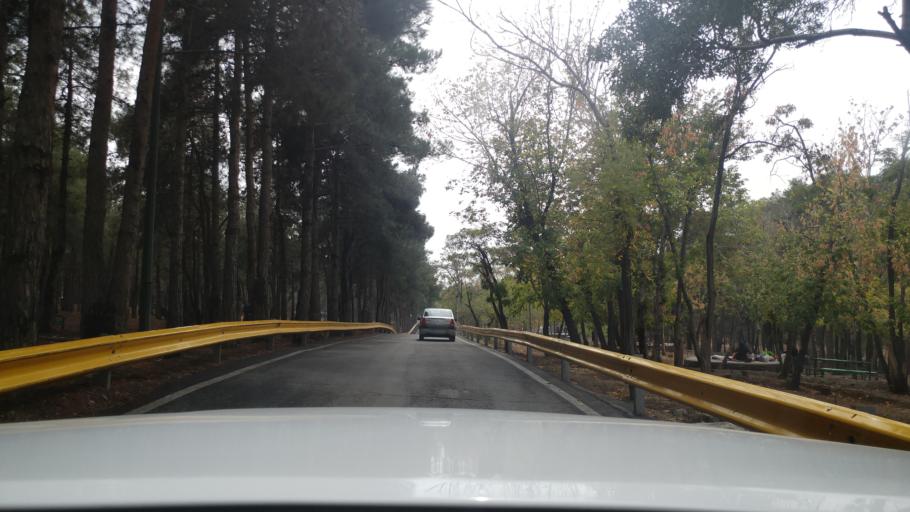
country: IR
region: Tehran
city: Shahr-e Qods
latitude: 35.7262
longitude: 51.2231
